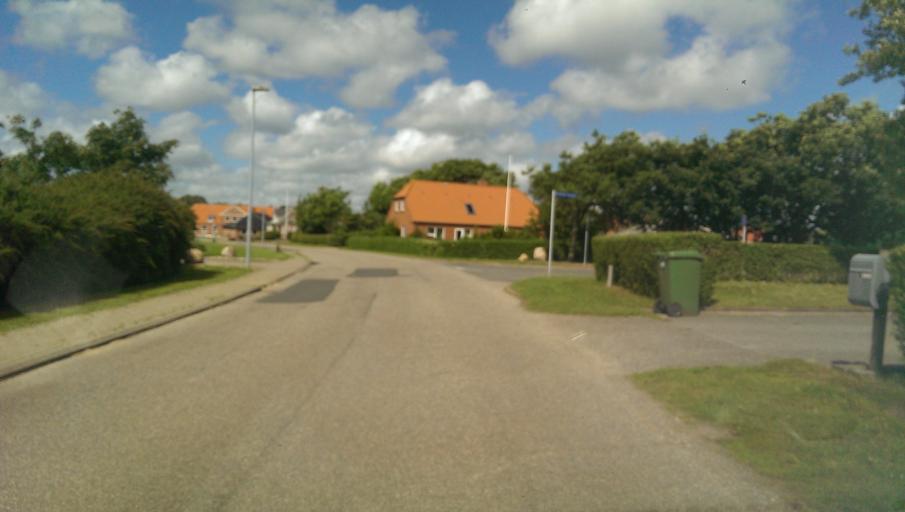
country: DK
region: Central Jutland
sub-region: Holstebro Kommune
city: Ulfborg
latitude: 56.2644
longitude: 8.2394
